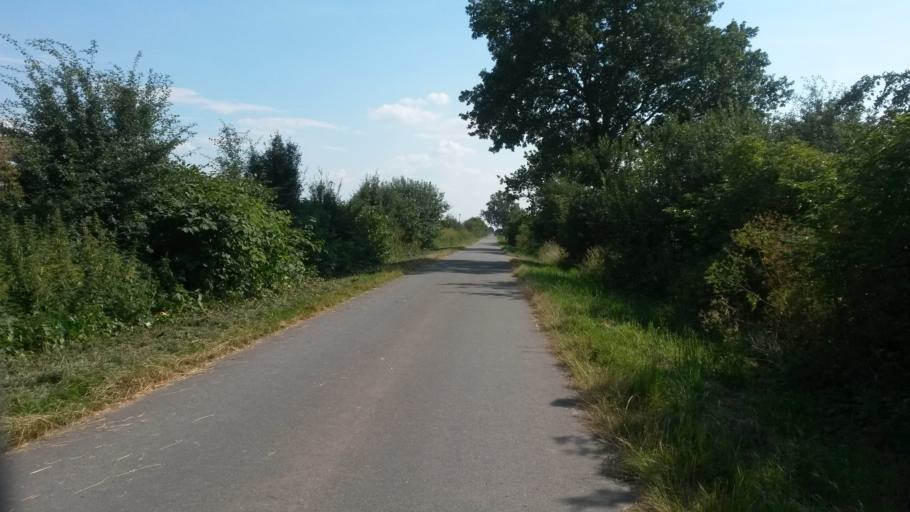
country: DE
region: Lower Saxony
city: Riede
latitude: 53.0313
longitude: 8.9123
